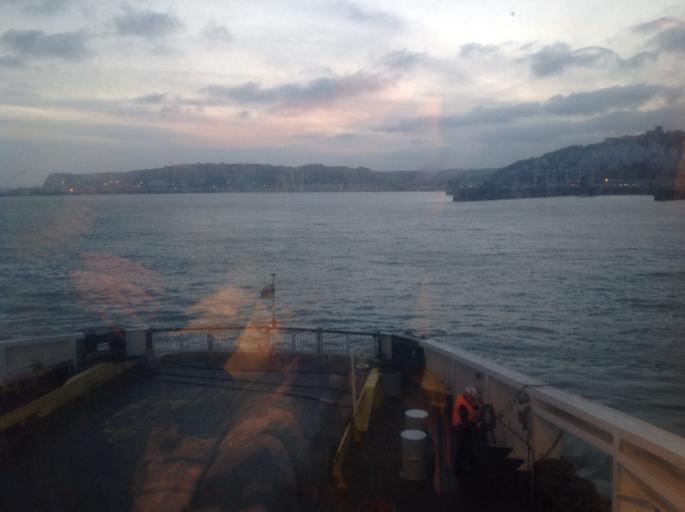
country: GB
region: England
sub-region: Kent
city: Dover
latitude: 51.1209
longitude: 1.3437
